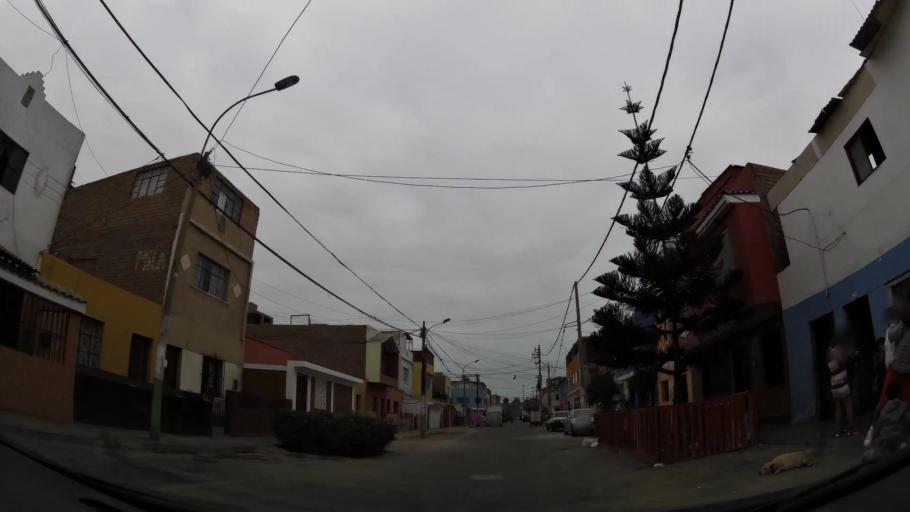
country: PE
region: Callao
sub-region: Callao
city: Callao
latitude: -12.0495
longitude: -77.1367
